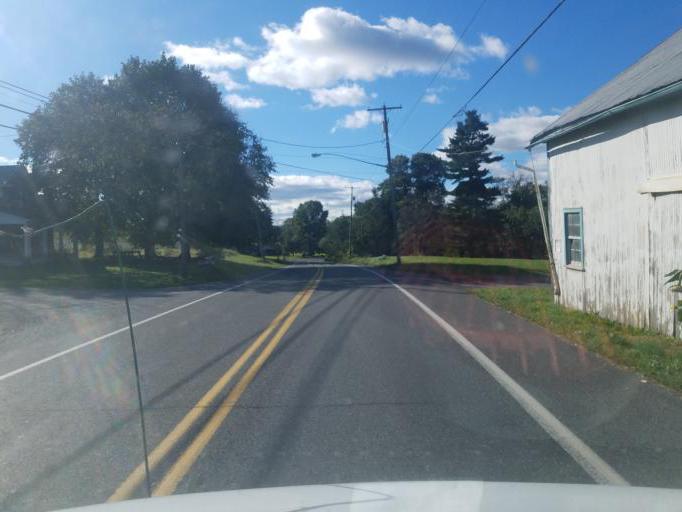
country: US
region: Pennsylvania
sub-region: Franklin County
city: Mont Alto
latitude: 39.8077
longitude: -77.5742
